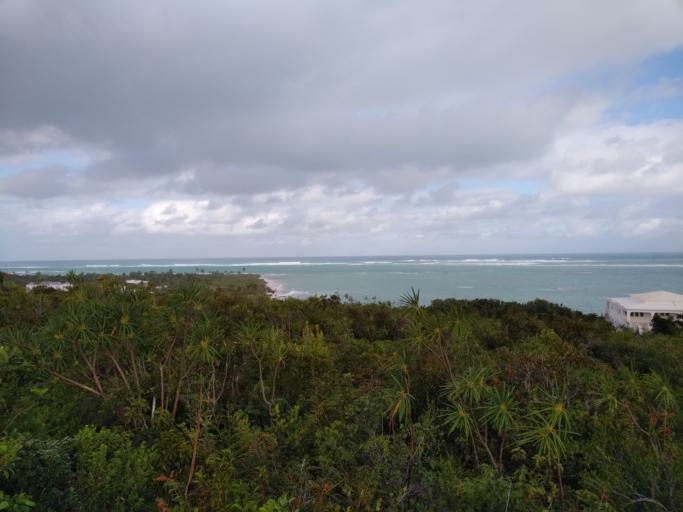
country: AI
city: Island Harbour
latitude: 18.2531
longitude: -63.0224
